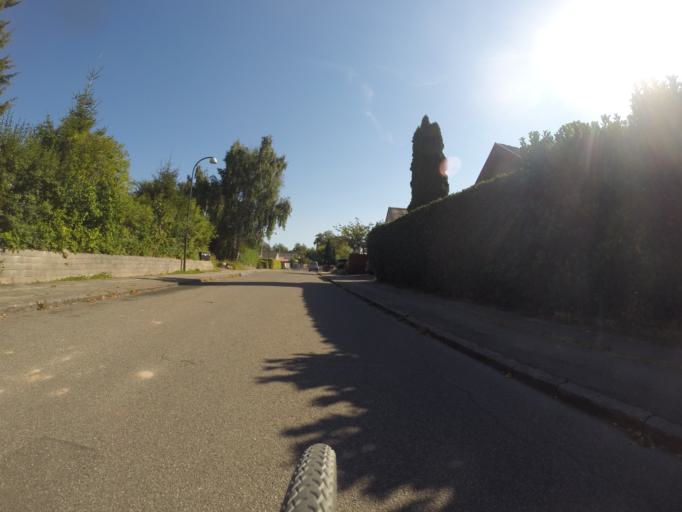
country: DK
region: Capital Region
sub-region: Herlev Kommune
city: Herlev
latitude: 55.7468
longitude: 12.4254
